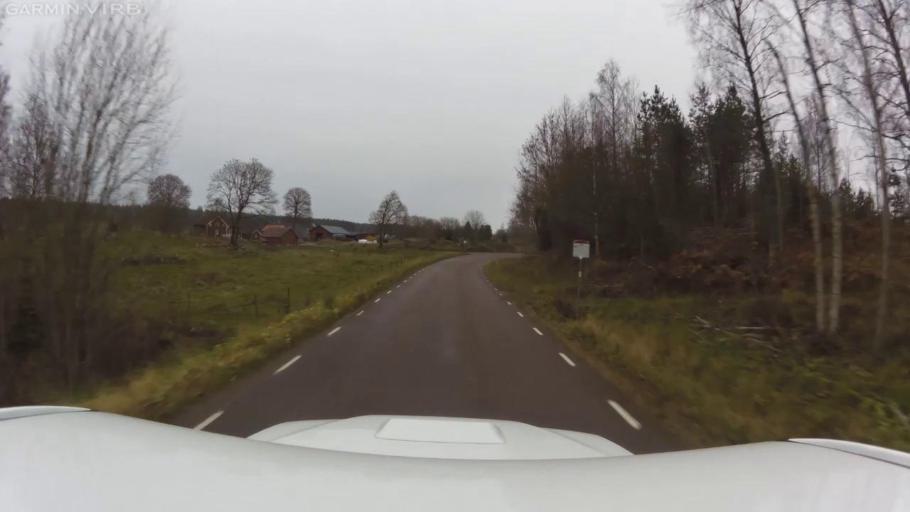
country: SE
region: OEstergoetland
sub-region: Mjolby Kommun
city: Mantorp
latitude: 58.1578
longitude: 15.3914
